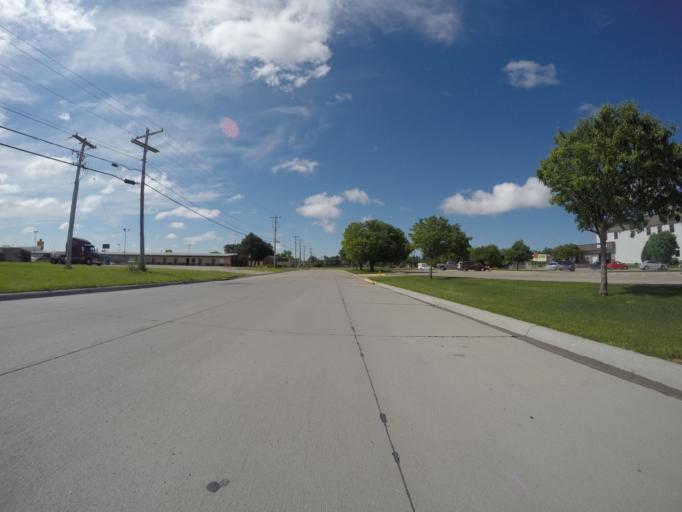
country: US
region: Nebraska
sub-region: Buffalo County
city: Kearney
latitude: 40.6794
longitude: -99.0876
